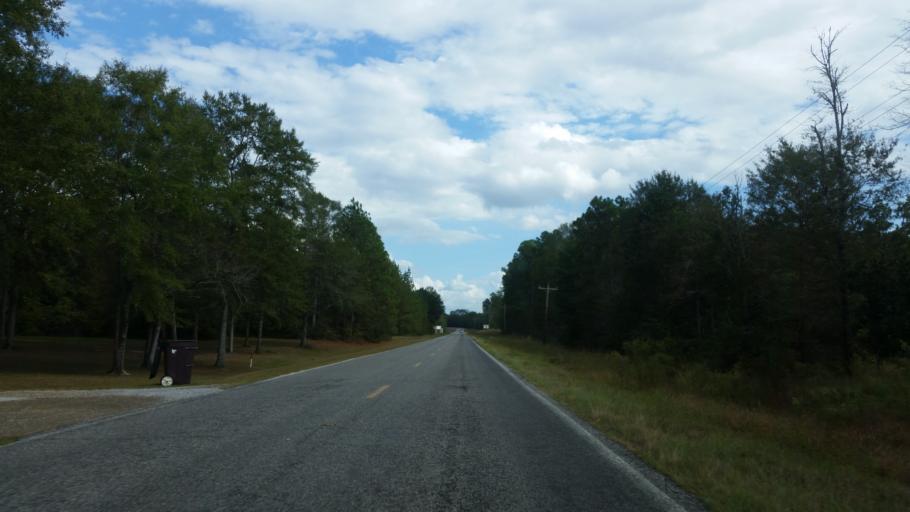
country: US
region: Mississippi
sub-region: Stone County
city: Wiggins
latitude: 30.9117
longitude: -89.0972
